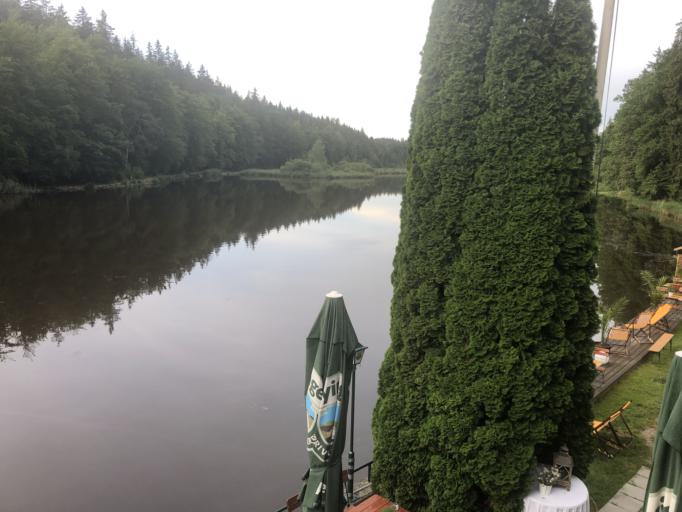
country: DE
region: Bavaria
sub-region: Upper Bavaria
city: Strasslach-Dingharting
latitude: 47.9672
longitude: 11.5245
